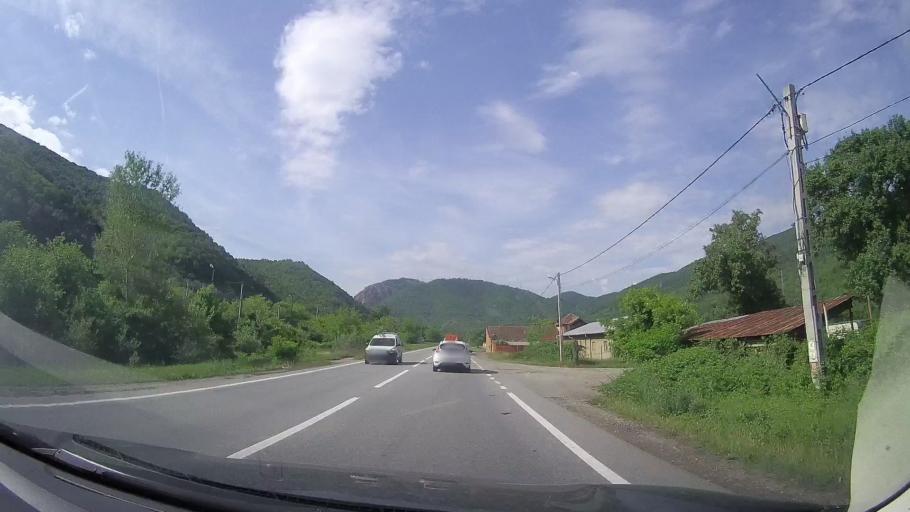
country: RO
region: Caras-Severin
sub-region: Oras Baile Herculane
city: Baile Herculane
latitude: 44.8769
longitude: 22.3845
